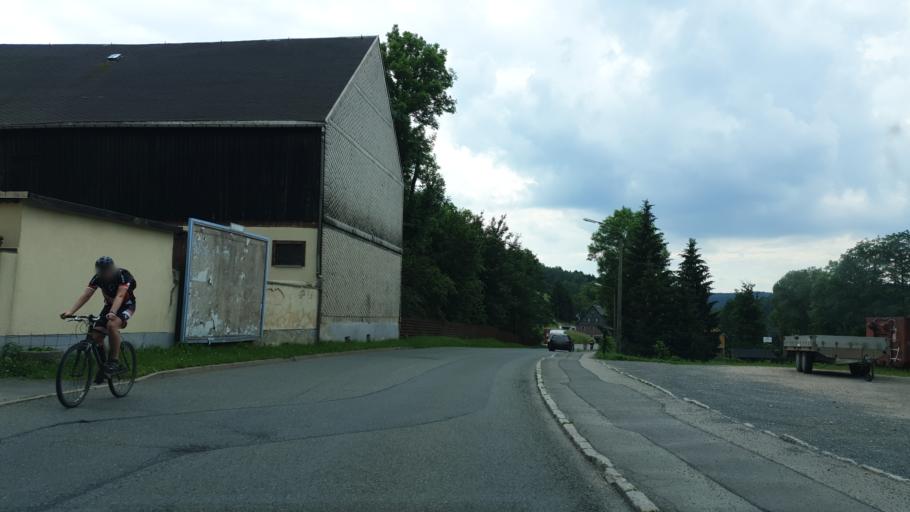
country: DE
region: Saxony
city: Aue
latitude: 50.6117
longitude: 12.7081
